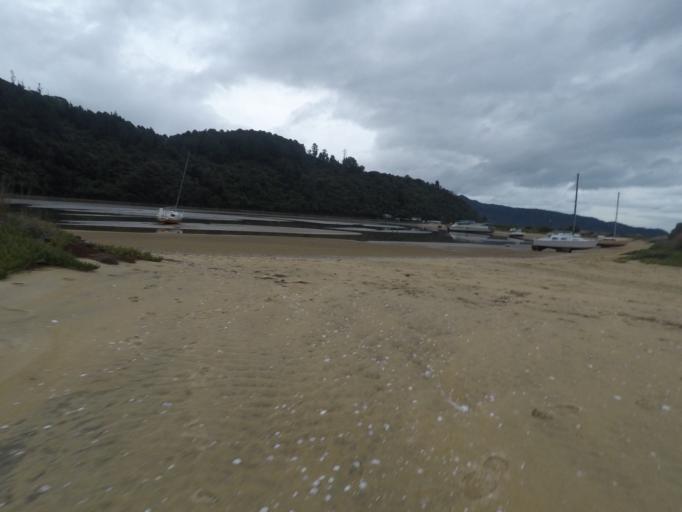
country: NZ
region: Tasman
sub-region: Tasman District
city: Motueka
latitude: -41.0125
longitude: 173.0063
